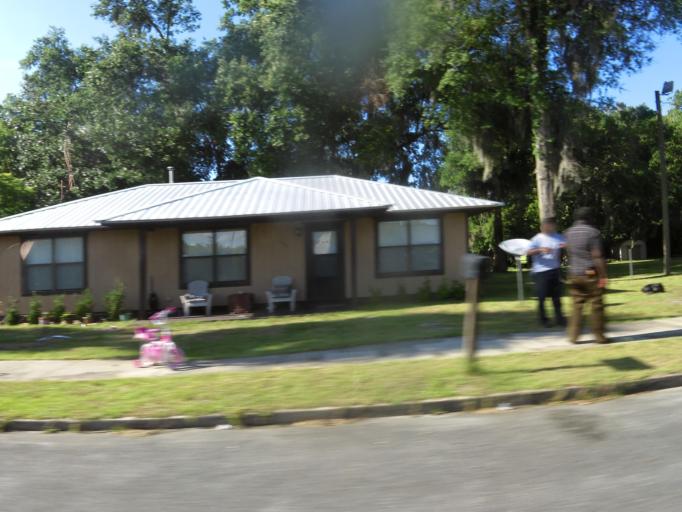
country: US
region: Florida
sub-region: Putnam County
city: Palatka
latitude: 29.6495
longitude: -81.6359
